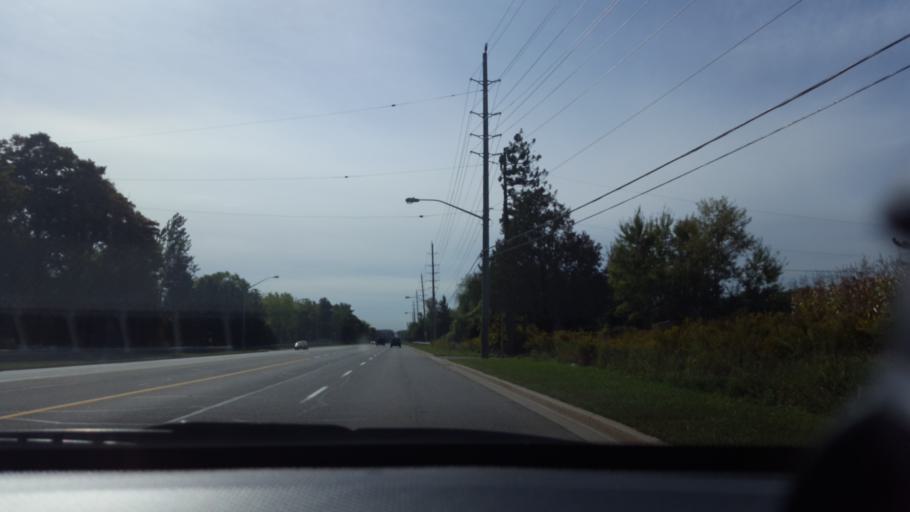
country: CA
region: Ontario
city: Newmarket
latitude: 44.0075
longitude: -79.4974
